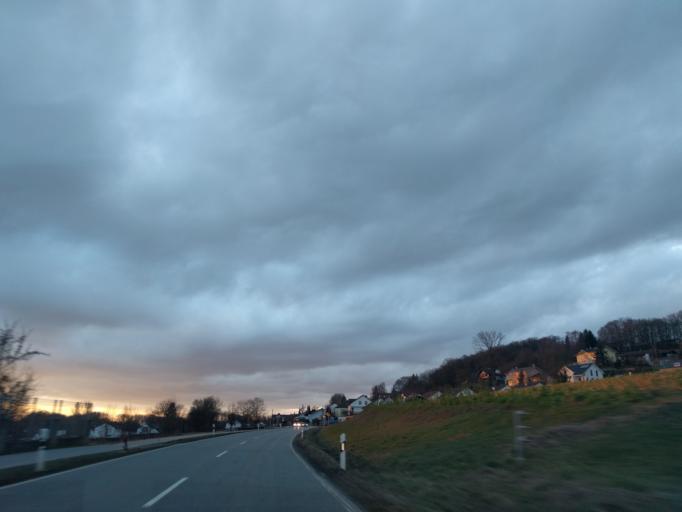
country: DE
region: Bavaria
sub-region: Lower Bavaria
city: Winzer
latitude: 48.7184
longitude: 13.0872
